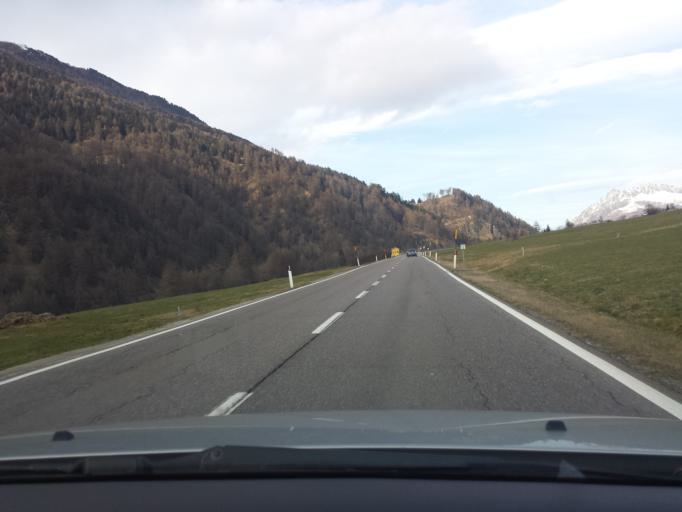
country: IT
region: Trentino-Alto Adige
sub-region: Bolzano
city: Malles Venosta
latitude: 46.7215
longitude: 10.5337
